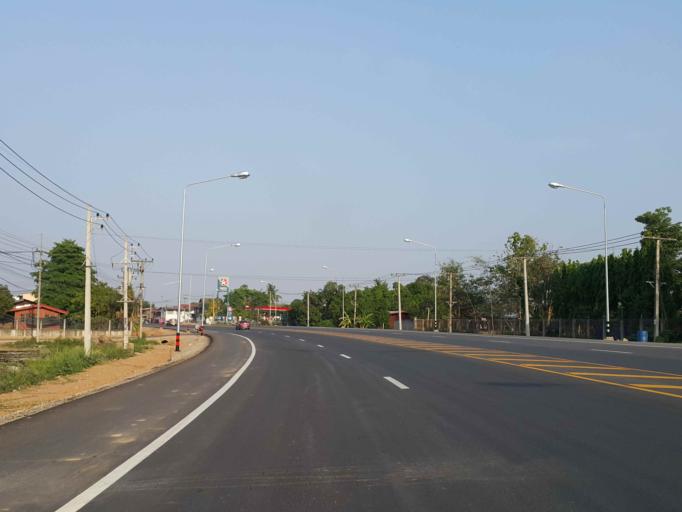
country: TH
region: Sukhothai
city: Sawankhalok
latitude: 17.3033
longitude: 99.8238
